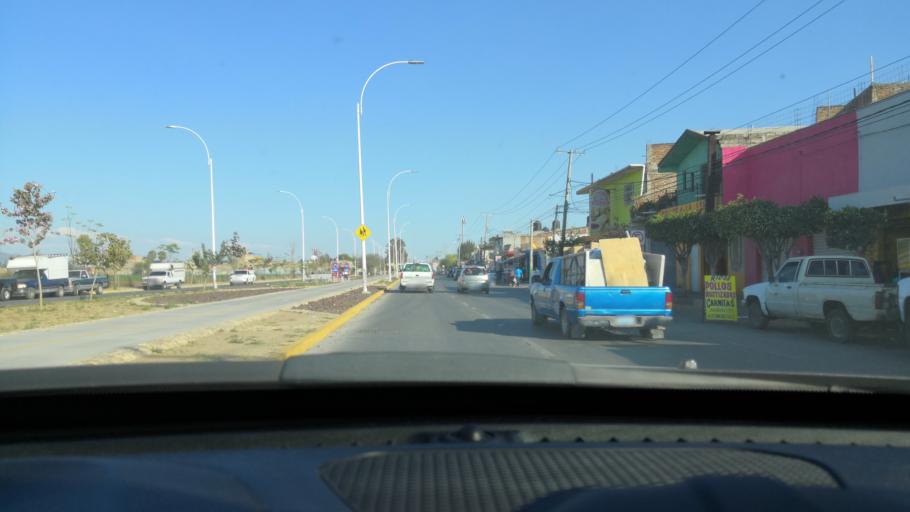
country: MX
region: Guanajuato
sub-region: Leon
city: San Jose de Duran (Los Troncoso)
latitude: 21.0626
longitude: -101.6241
